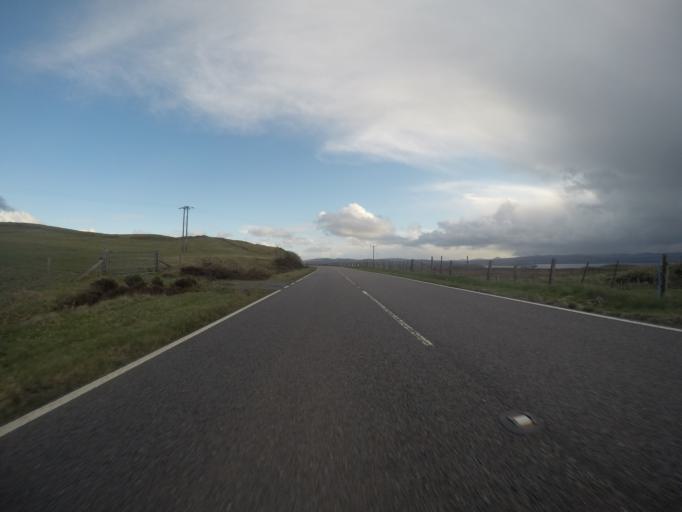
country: GB
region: Scotland
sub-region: Highland
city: Portree
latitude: 57.5538
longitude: -6.3656
